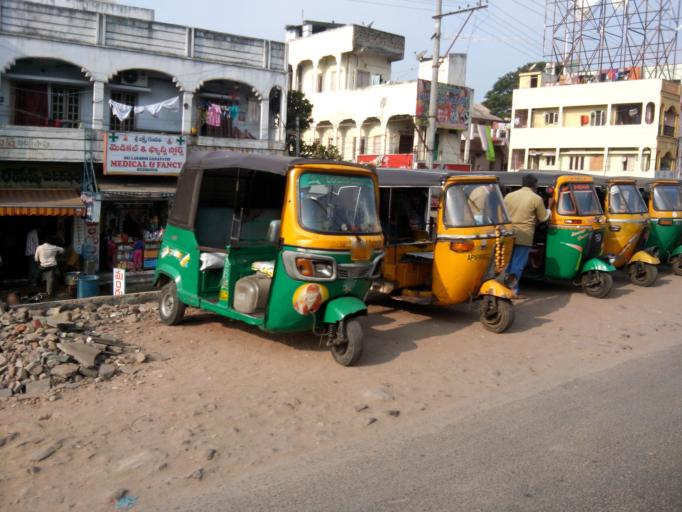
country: IN
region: Andhra Pradesh
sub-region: Krishna
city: Vijayawada
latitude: 16.5061
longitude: 80.6270
